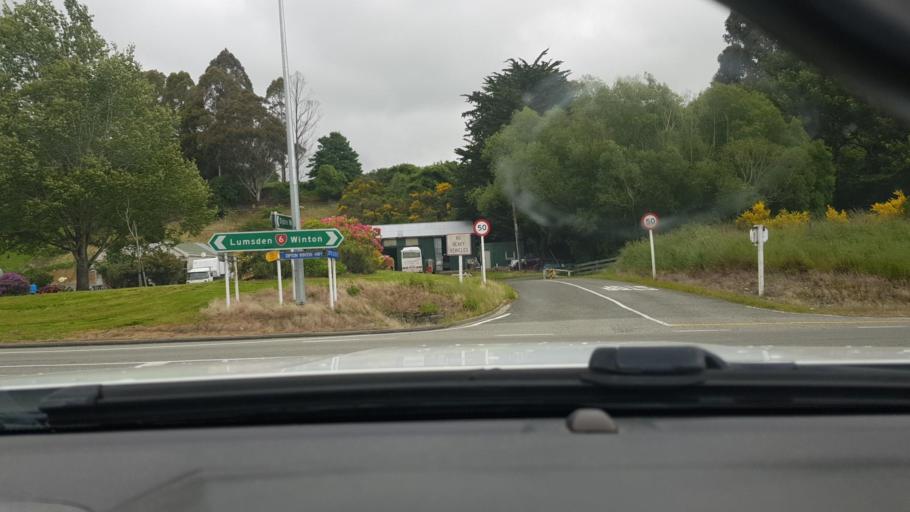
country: NZ
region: Southland
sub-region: Southland District
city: Winton
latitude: -45.8986
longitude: 168.3669
